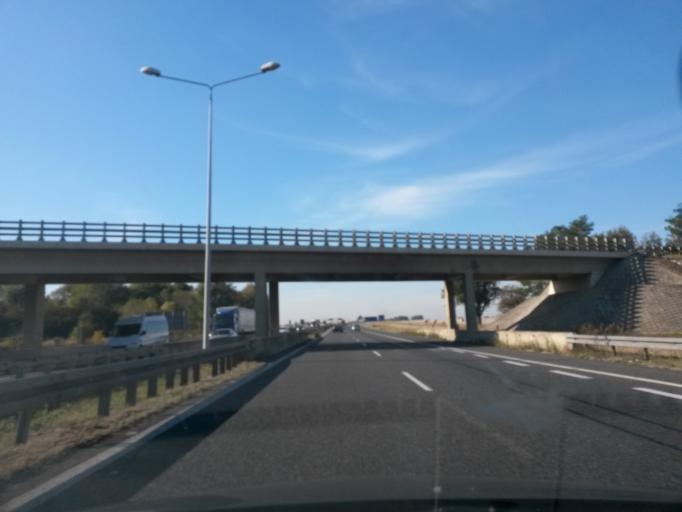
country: PL
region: Opole Voivodeship
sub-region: Powiat brzeski
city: Grodkow
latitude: 50.7839
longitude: 17.3454
